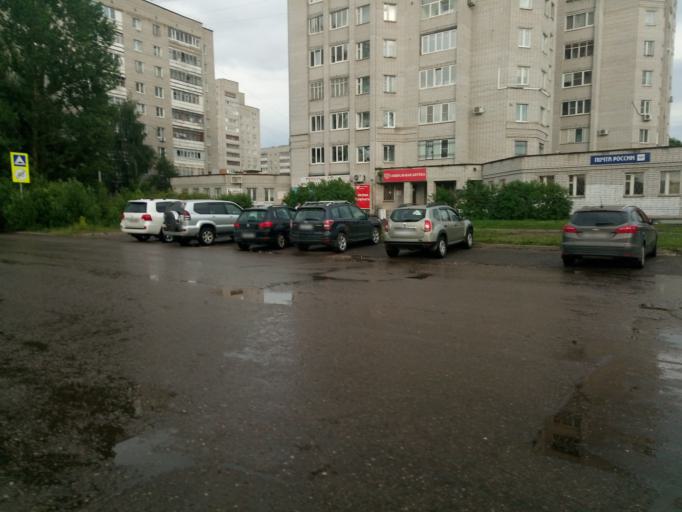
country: RU
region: Jaroslavl
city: Yaroslavl
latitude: 57.6438
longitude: 39.9524
